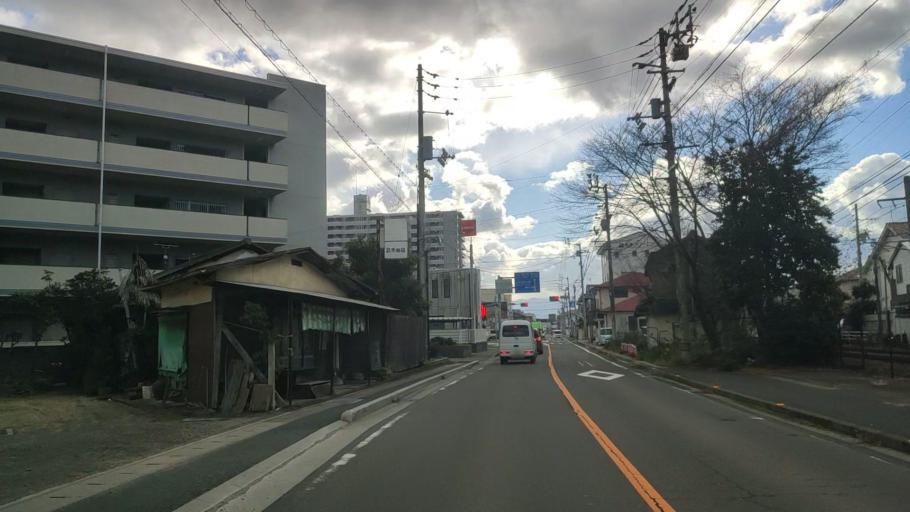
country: JP
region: Ehime
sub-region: Shikoku-chuo Shi
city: Matsuyama
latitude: 33.8685
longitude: 132.7176
